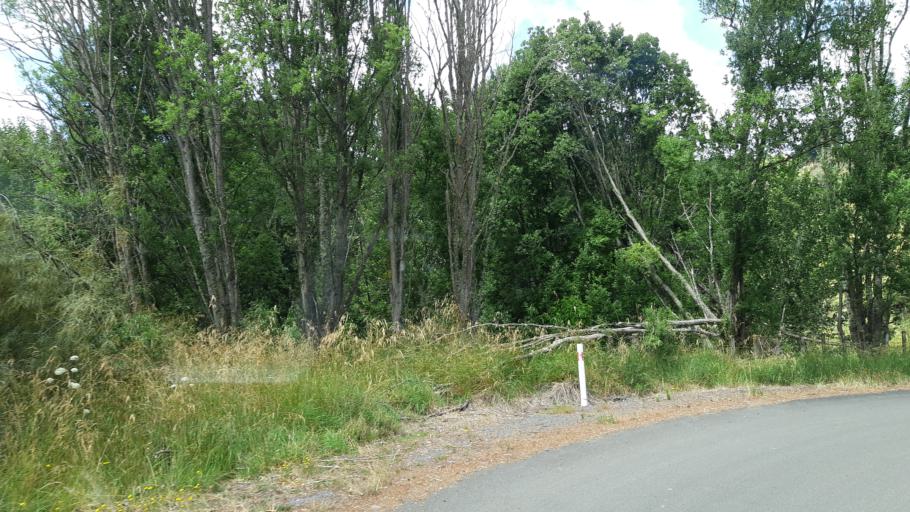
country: NZ
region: Manawatu-Wanganui
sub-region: Ruapehu District
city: Waiouru
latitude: -39.7874
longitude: 175.8931
